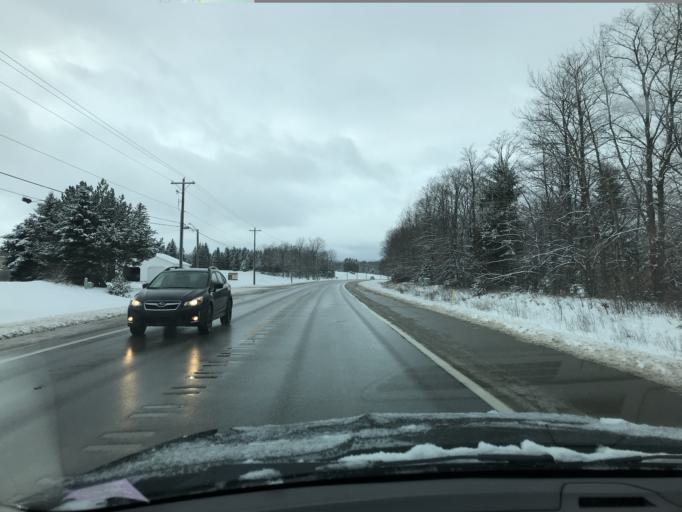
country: US
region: Michigan
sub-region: Charlevoix County
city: Charlevoix
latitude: 45.2812
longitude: -85.2354
